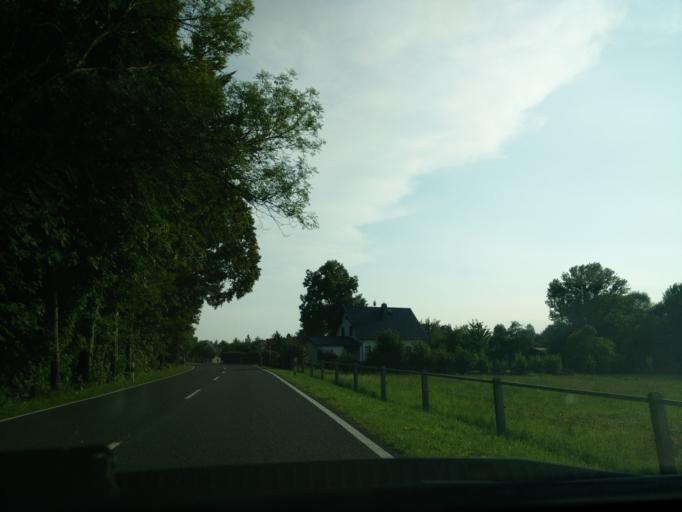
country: DE
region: Saxony
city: Frohburg
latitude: 51.0729
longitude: 12.5595
